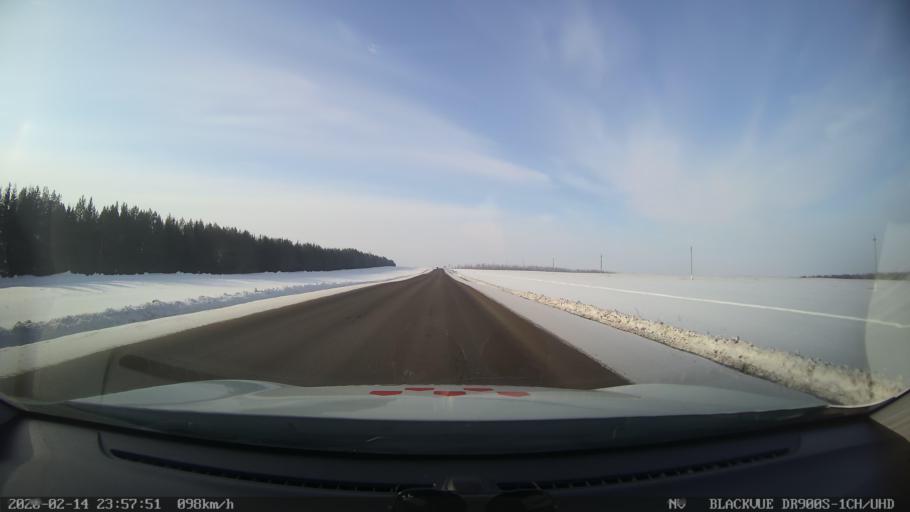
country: RU
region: Tatarstan
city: Kuybyshevskiy Zaton
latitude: 55.3370
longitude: 49.1000
